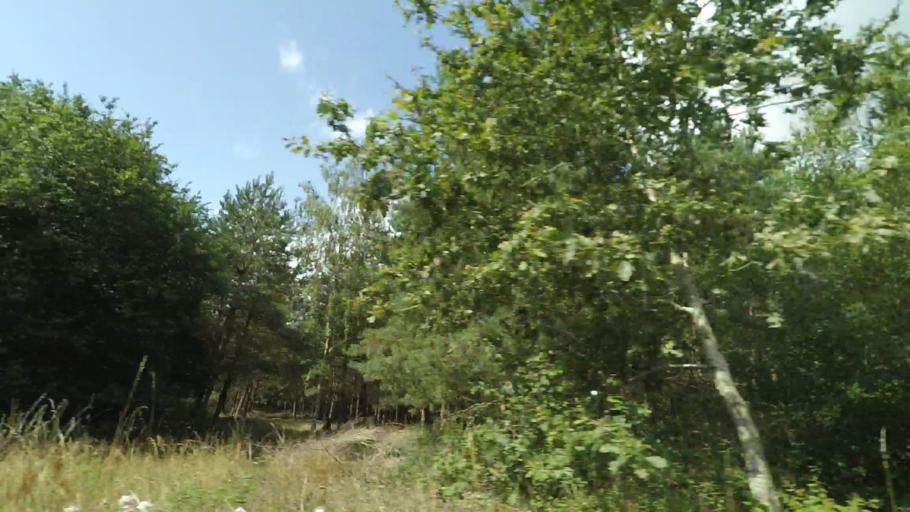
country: DK
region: Central Jutland
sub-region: Norddjurs Kommune
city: Allingabro
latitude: 56.5106
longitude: 10.3953
